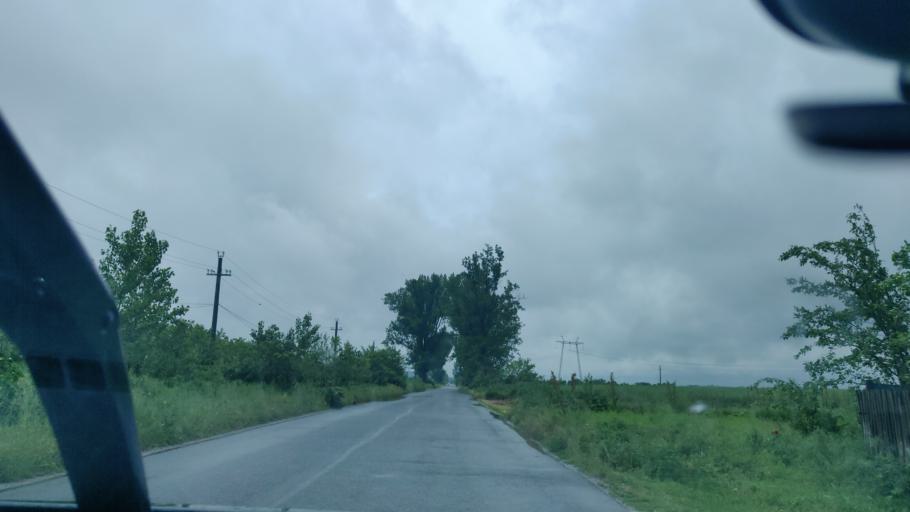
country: RO
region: Giurgiu
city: Iepuresti
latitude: 44.2685
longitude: 25.8479
